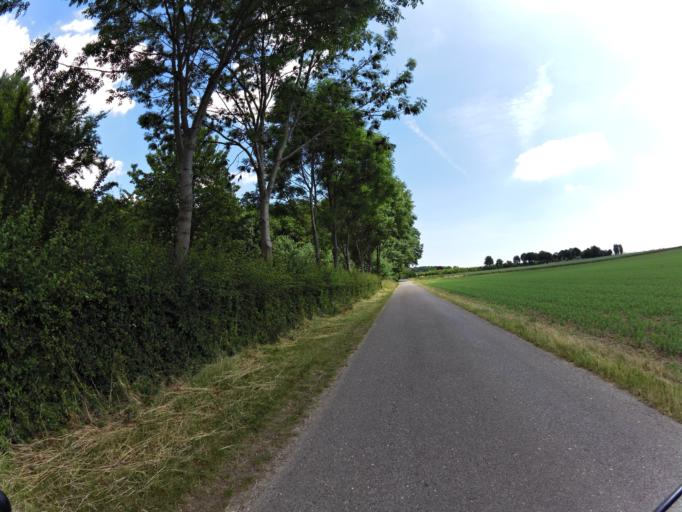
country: NL
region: Limburg
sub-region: Gemeente Echt-Susteren
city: Koningsbosch
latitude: 51.0270
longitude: 5.9603
